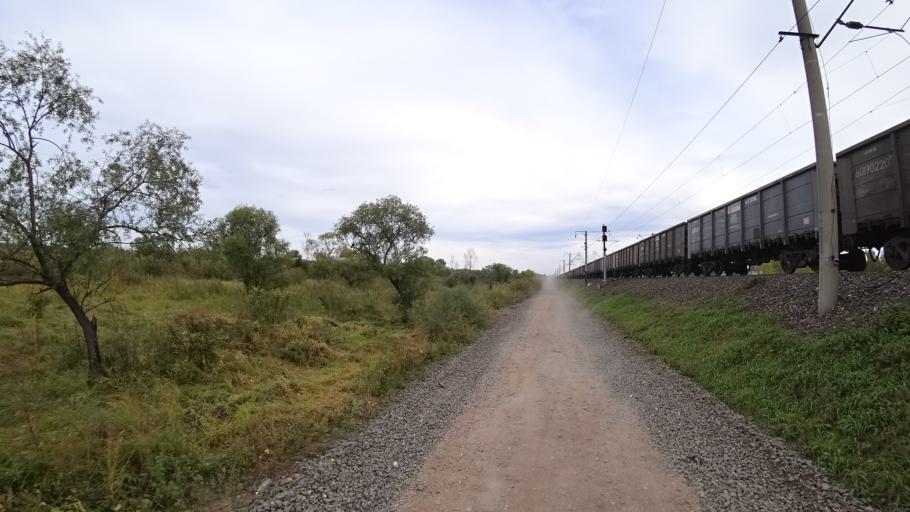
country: RU
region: Amur
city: Arkhara
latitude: 49.3577
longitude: 130.1524
